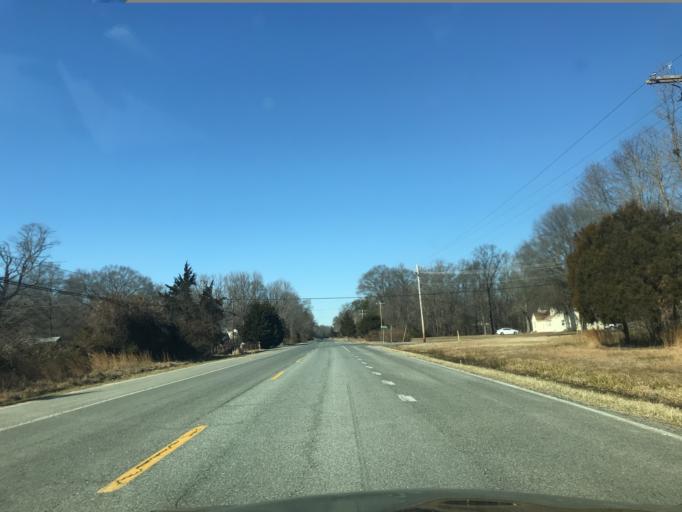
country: US
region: Maryland
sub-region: Charles County
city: Bryans Road
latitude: 38.6646
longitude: -77.0814
